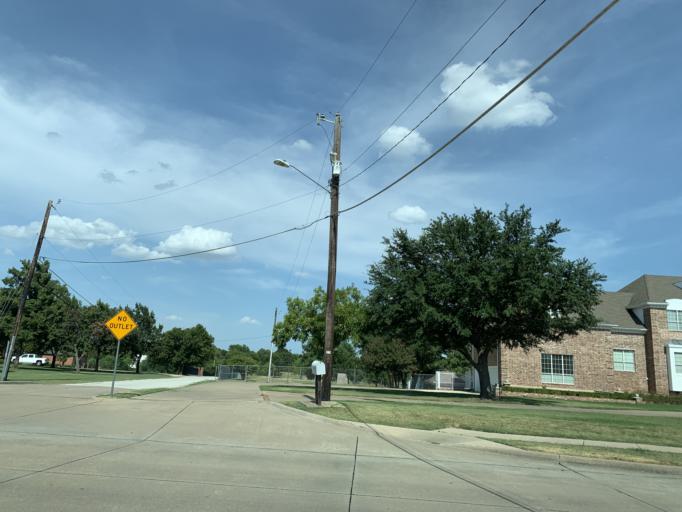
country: US
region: Texas
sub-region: Dallas County
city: Cedar Hill
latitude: 32.6527
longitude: -97.0075
